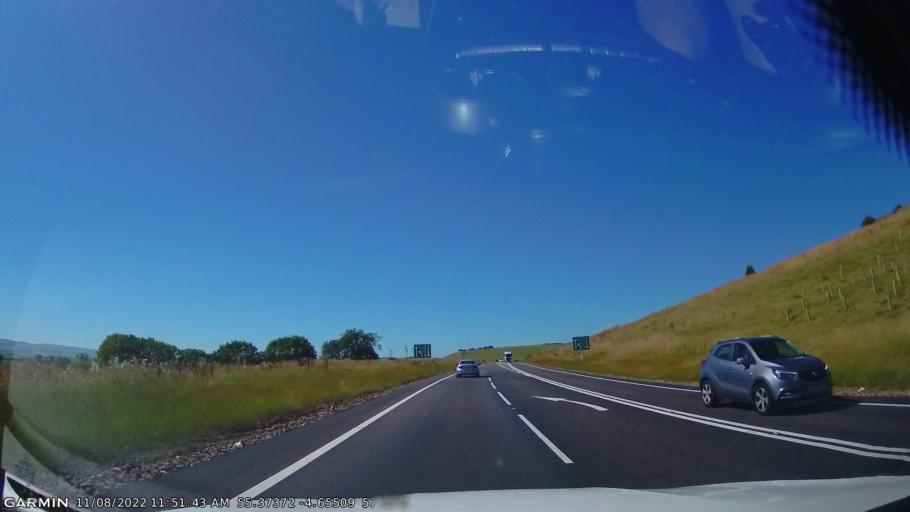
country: GB
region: Scotland
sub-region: South Ayrshire
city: Maybole
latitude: 55.3739
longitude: -4.6548
